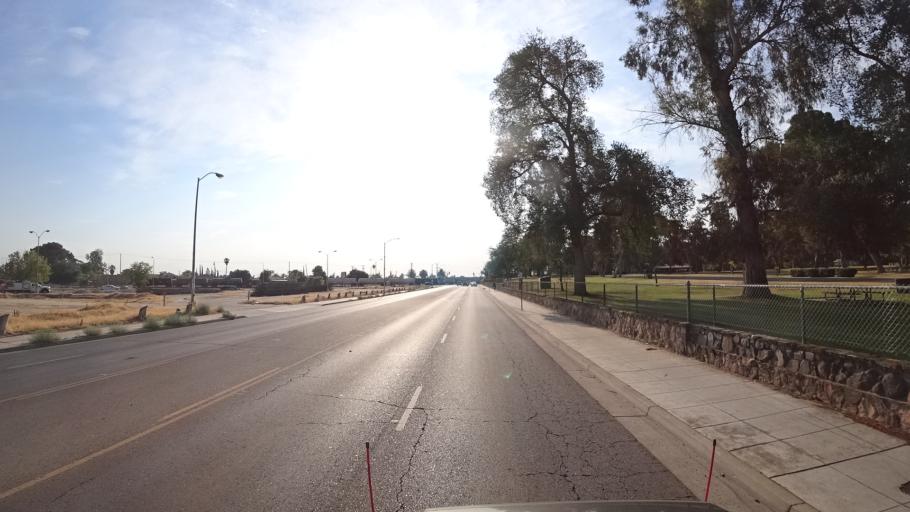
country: US
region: California
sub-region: Fresno County
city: Fresno
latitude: 36.7575
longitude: -119.8240
